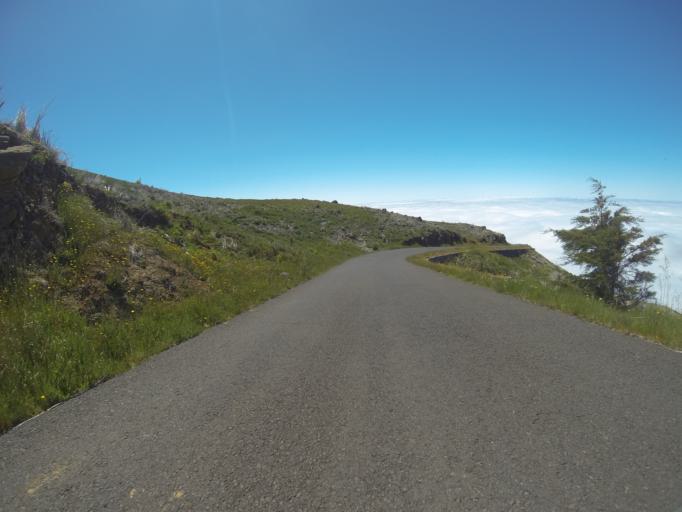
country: PT
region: Madeira
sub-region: Funchal
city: Nossa Senhora do Monte
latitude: 32.7061
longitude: -16.9147
